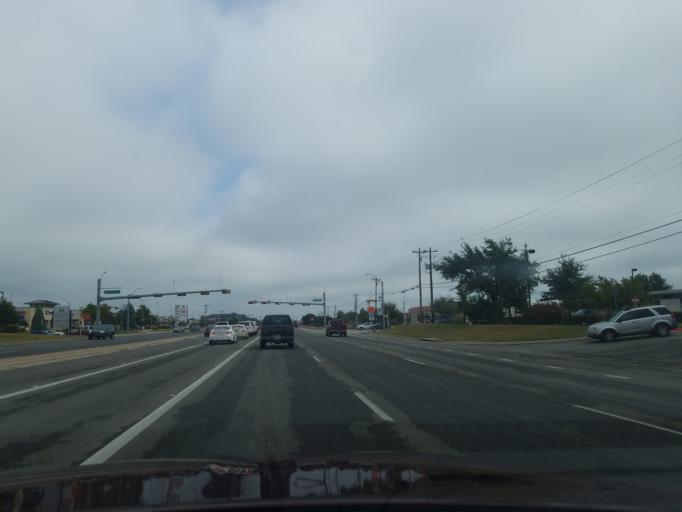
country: US
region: Texas
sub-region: Williamson County
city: Cedar Park
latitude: 30.5264
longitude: -97.8122
